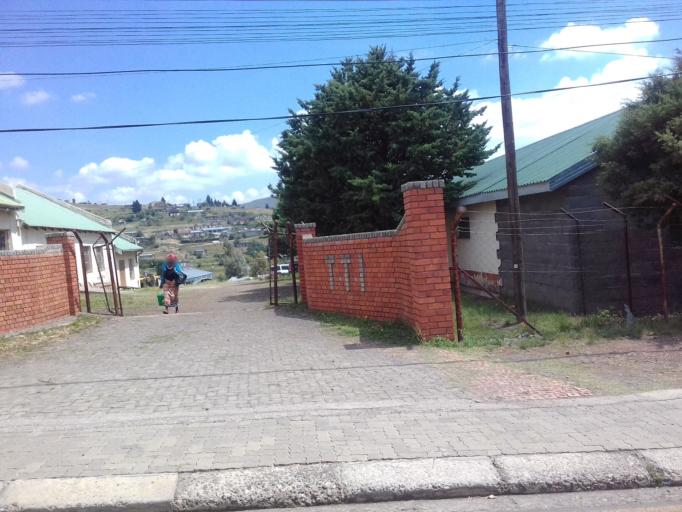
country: LS
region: Thaba-Tseka
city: Thaba-Tseka
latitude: -29.5206
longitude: 28.6087
